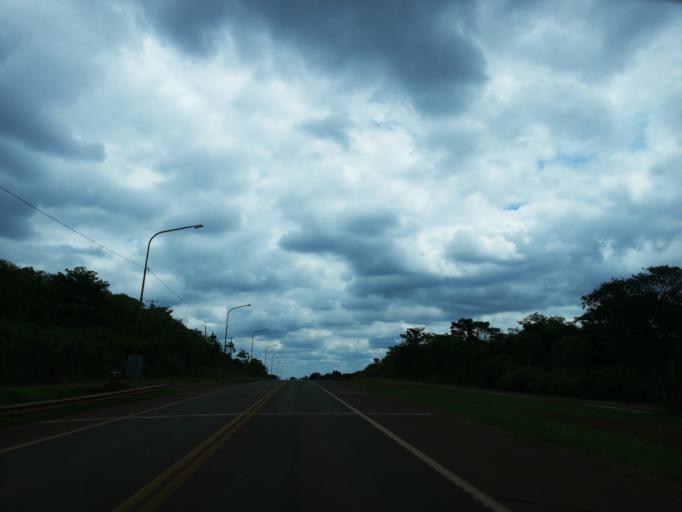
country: AR
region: Misiones
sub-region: Departamento de Leandro N. Alem
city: Leandro N. Alem
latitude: -27.6162
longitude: -55.3220
